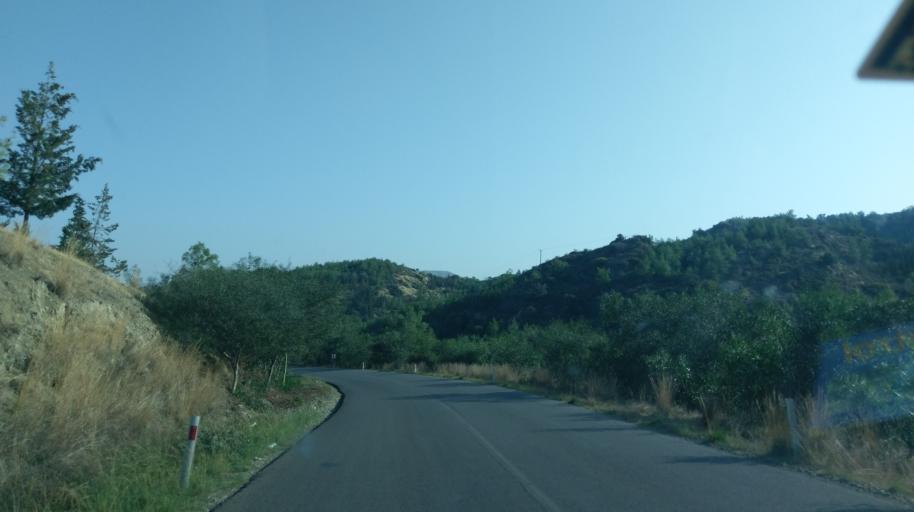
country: CY
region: Lefkosia
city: Kato Pyrgos
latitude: 35.1551
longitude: 32.7706
